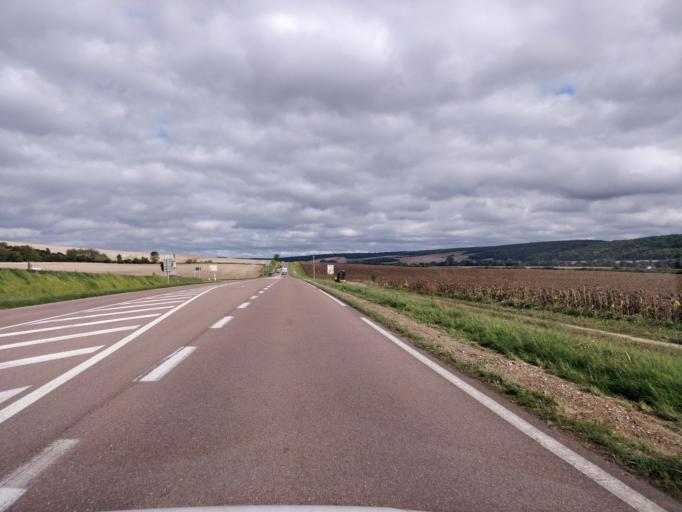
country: FR
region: Champagne-Ardenne
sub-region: Departement de l'Aube
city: Aix-en-Othe
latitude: 48.2333
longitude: 3.6299
